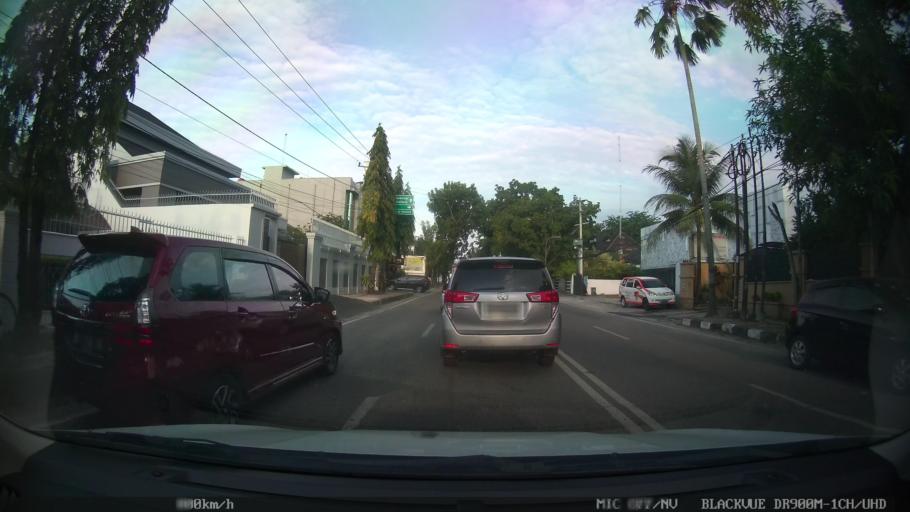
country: ID
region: North Sumatra
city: Medan
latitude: 3.5769
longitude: 98.6598
